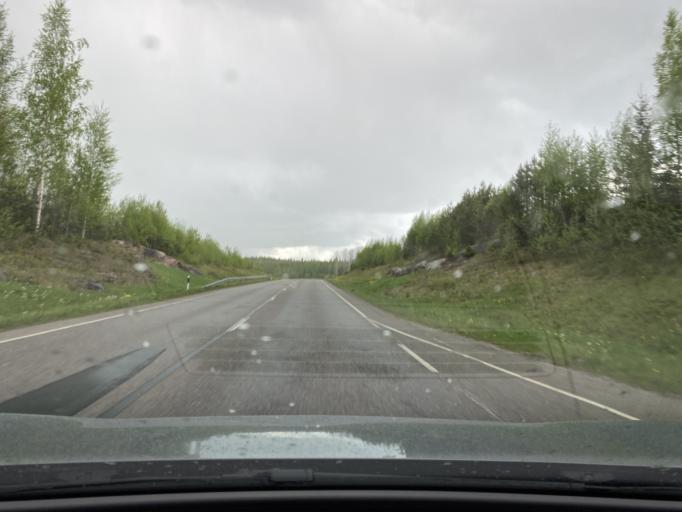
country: FI
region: Paijanne Tavastia
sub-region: Lahti
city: Jaervelae
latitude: 60.7842
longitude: 25.4081
